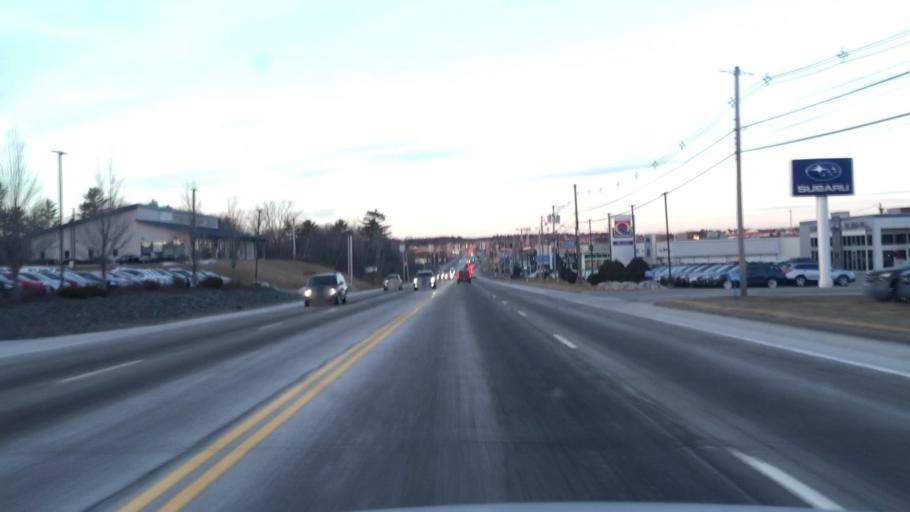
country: US
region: Maine
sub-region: Penobscot County
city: Brewer
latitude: 44.8237
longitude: -68.7399
